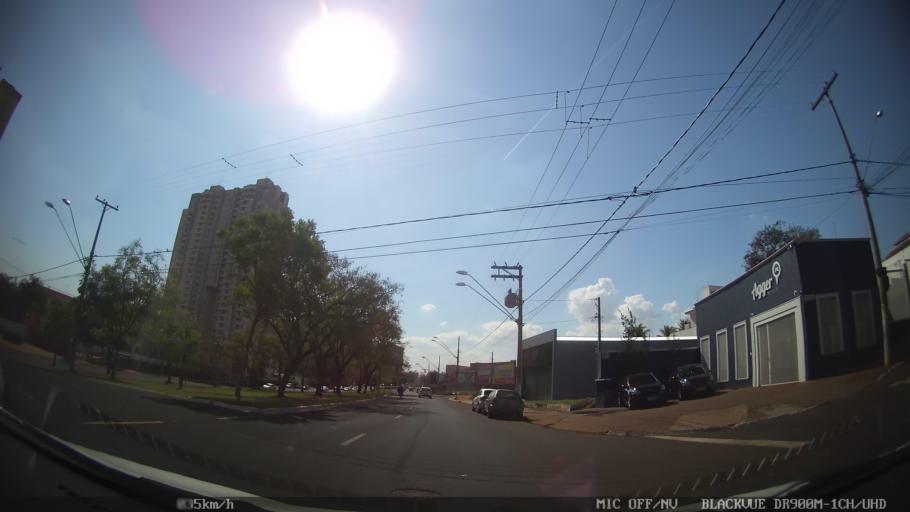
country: BR
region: Sao Paulo
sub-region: Ribeirao Preto
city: Ribeirao Preto
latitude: -21.2013
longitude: -47.8230
